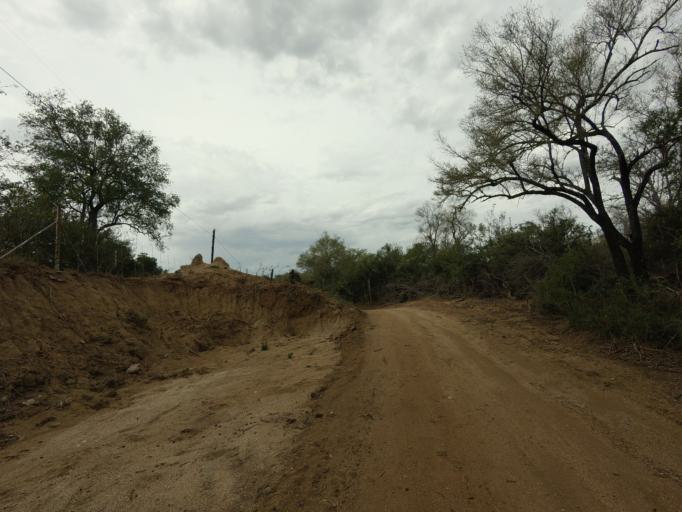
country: ZA
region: Limpopo
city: Thulamahashi
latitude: -24.5202
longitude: 31.1122
